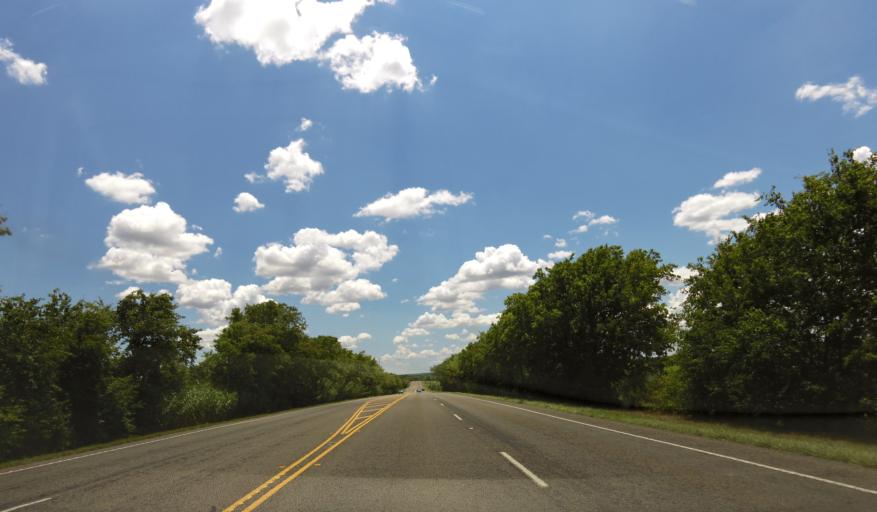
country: US
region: Texas
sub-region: Bastrop County
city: Camp Swift
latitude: 30.1866
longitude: -97.1657
